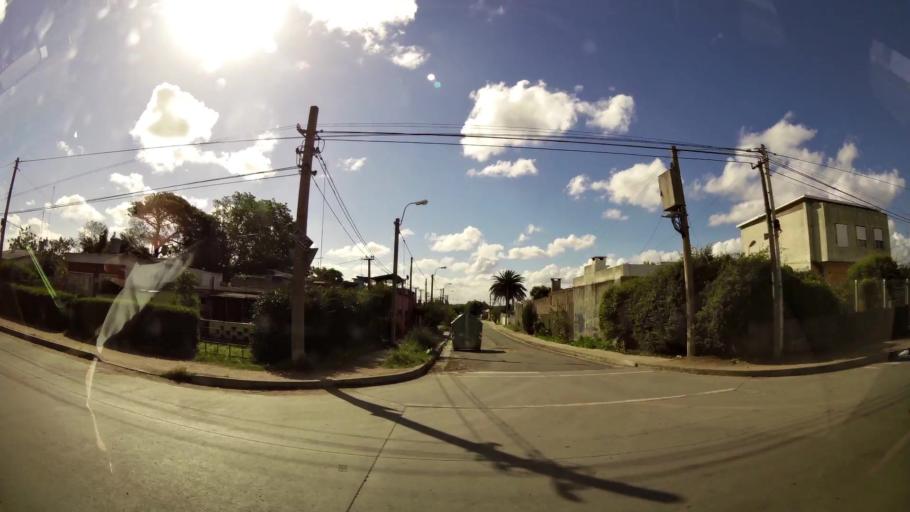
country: UY
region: Canelones
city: La Paz
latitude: -34.8121
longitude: -56.2293
